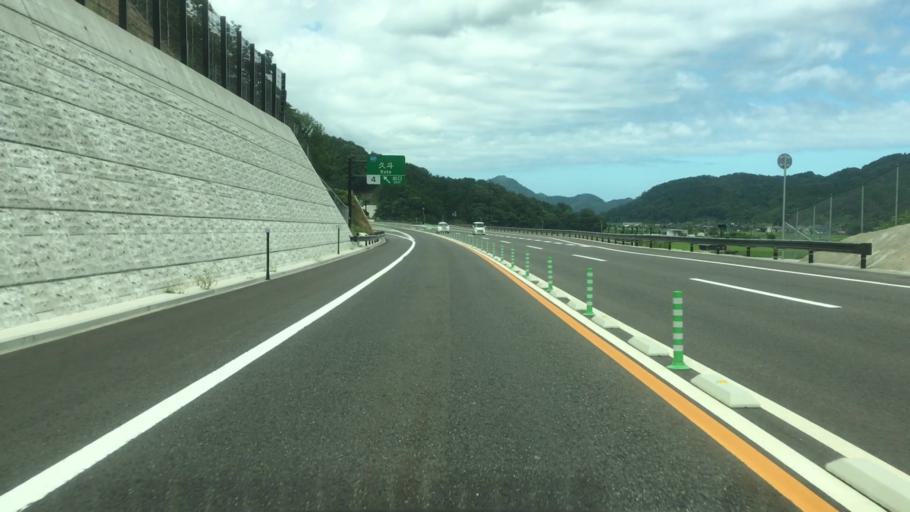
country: JP
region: Tottori
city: Tottori
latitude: 35.6221
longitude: 134.5046
